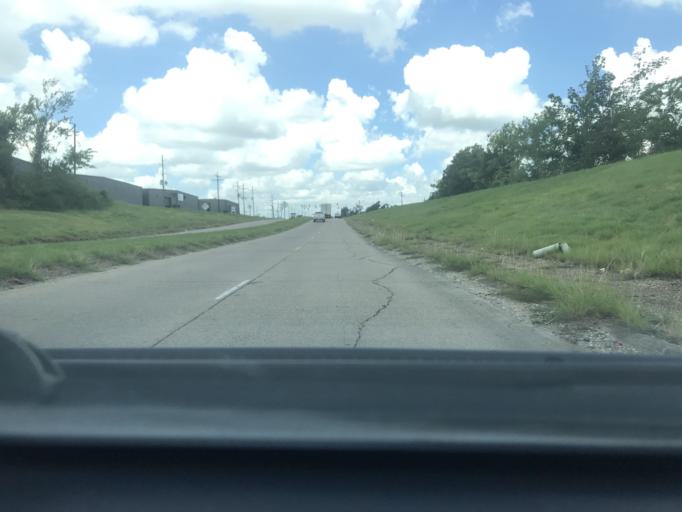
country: US
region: Louisiana
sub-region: Calcasieu Parish
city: Westlake
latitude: 30.2373
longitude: -93.2830
